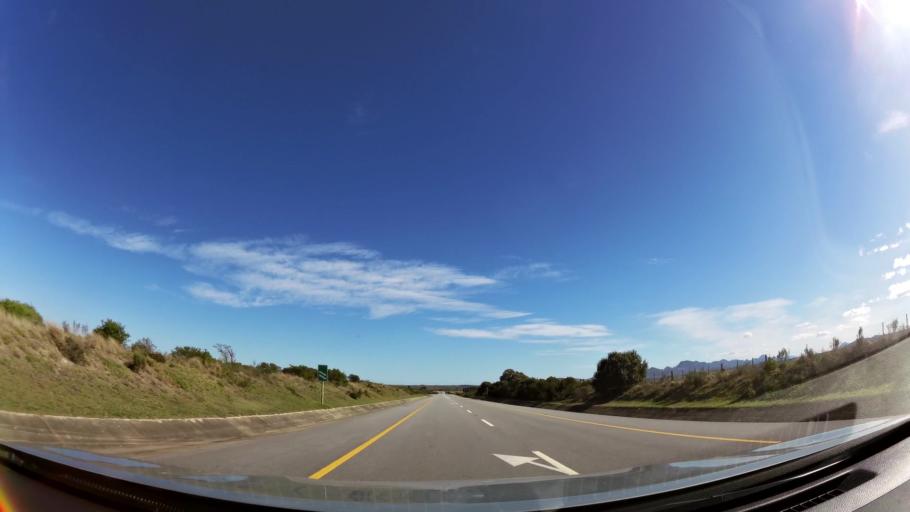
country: ZA
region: Eastern Cape
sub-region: Cacadu District Municipality
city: Kruisfontein
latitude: -34.0251
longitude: 24.6083
